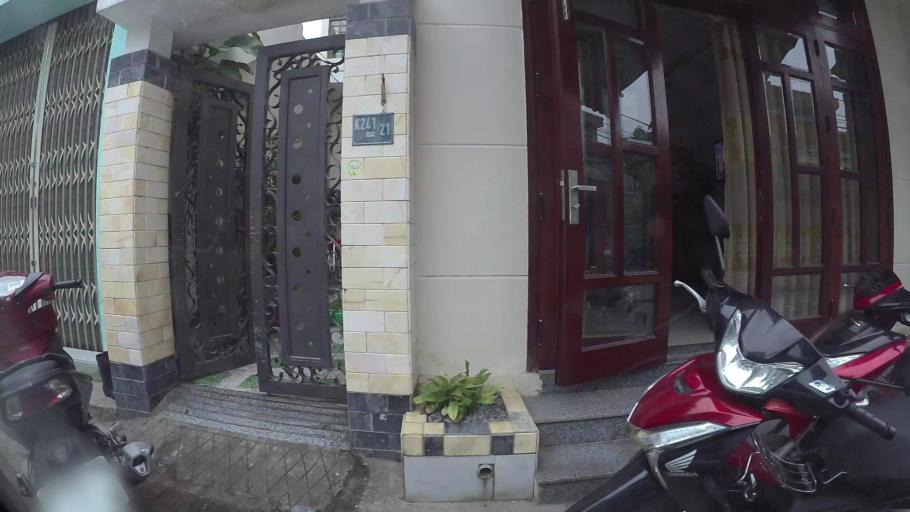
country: VN
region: Da Nang
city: Thanh Khe
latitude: 16.0552
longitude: 108.1838
